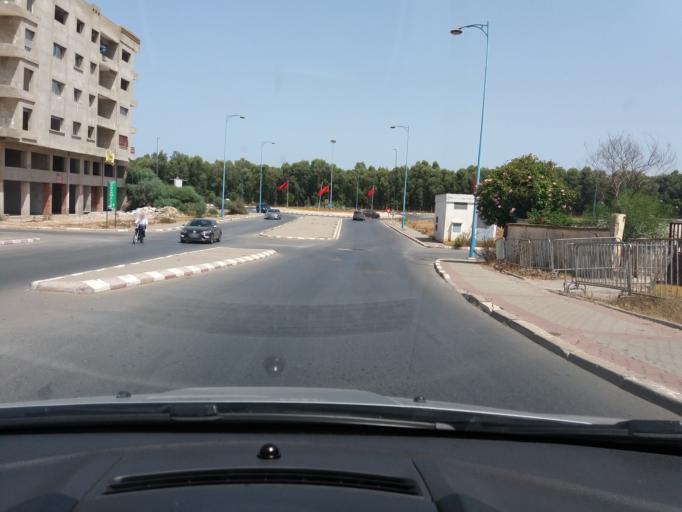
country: MA
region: Gharb-Chrarda-Beni Hssen
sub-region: Kenitra Province
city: Kenitra
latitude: 34.2719
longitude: -6.6210
